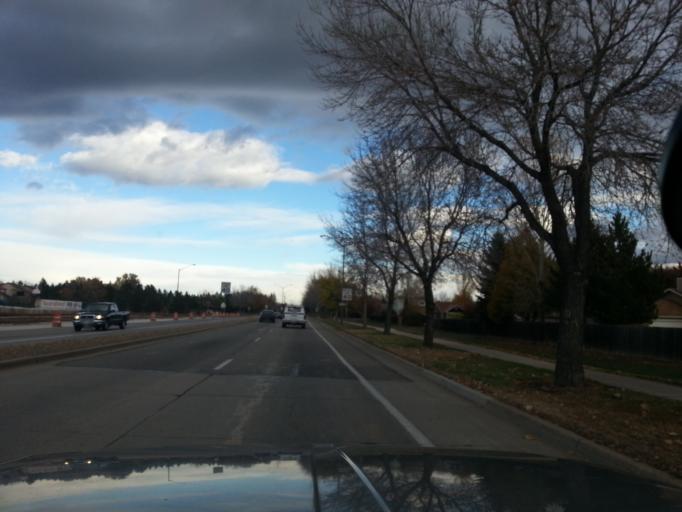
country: US
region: Colorado
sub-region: Larimer County
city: Fort Collins
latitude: 40.5386
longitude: -105.1151
